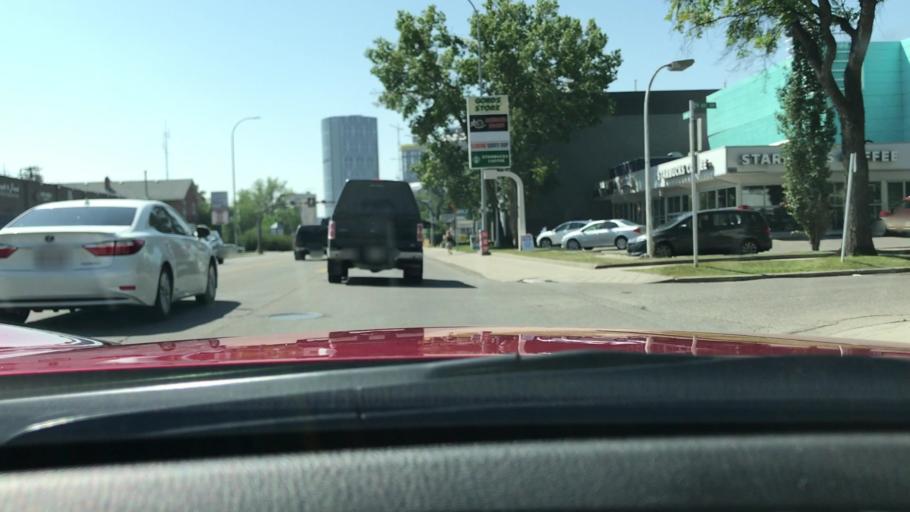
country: CA
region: Alberta
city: Calgary
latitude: 51.0607
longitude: -114.0626
